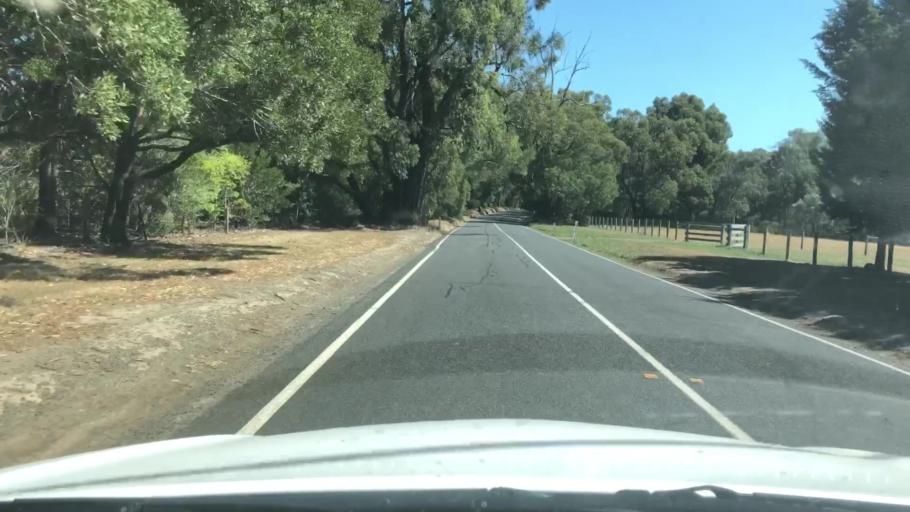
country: AU
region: Victoria
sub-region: Yarra Ranges
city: Woori Yallock
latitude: -37.8225
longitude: 145.4950
